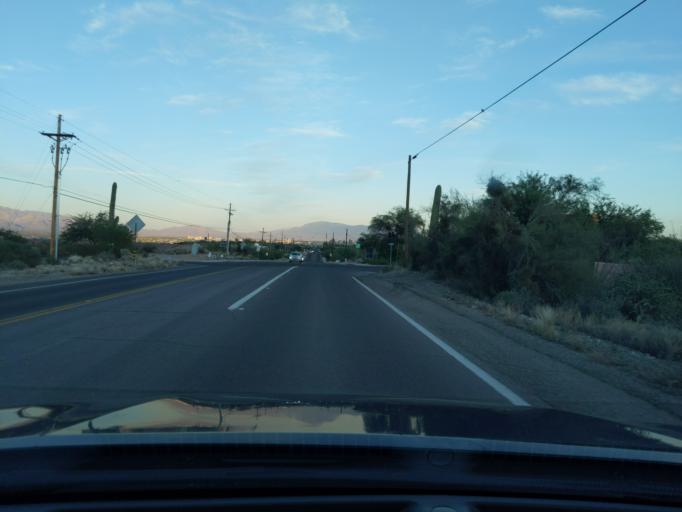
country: US
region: Arizona
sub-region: Pima County
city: Tucson Estates
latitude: 32.2249
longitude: -111.0344
